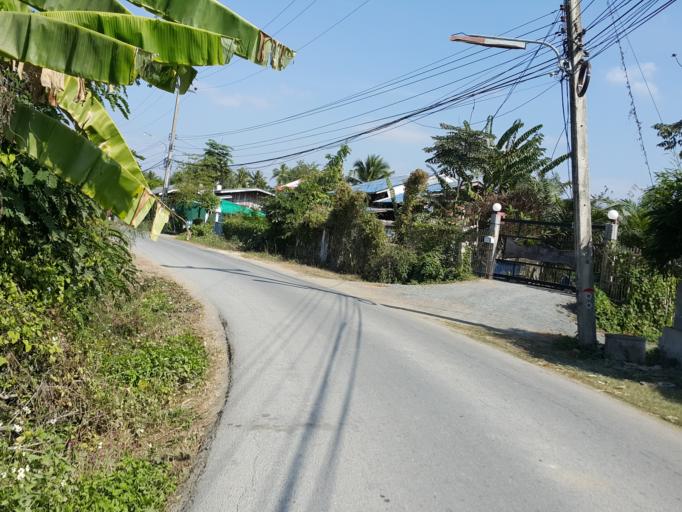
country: TH
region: Chiang Mai
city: San Kamphaeng
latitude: 18.8054
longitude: 99.1503
